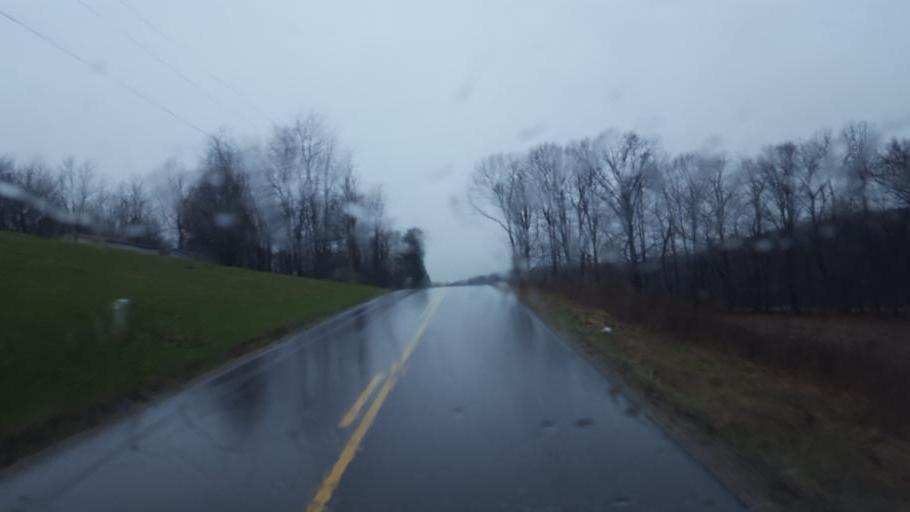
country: US
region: Ohio
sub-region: Knox County
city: Gambier
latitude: 40.4284
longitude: -82.4313
